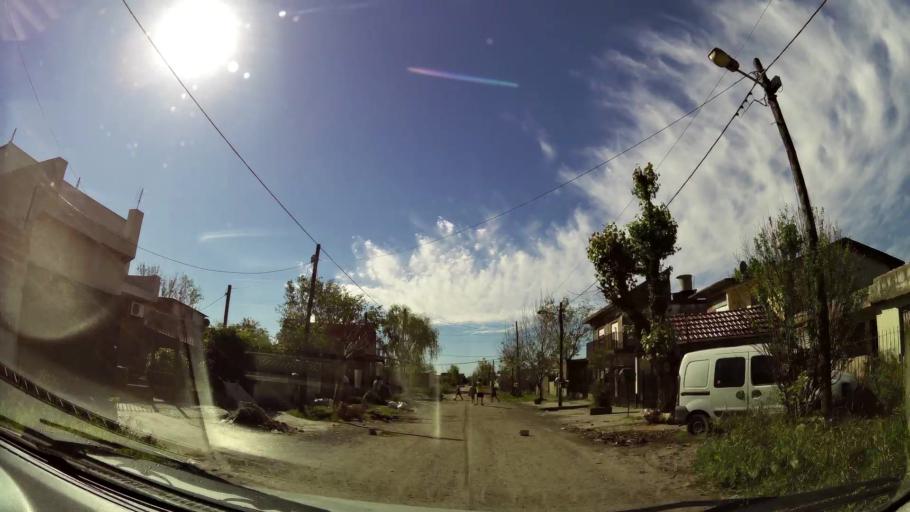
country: AR
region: Buenos Aires
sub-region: Partido de Quilmes
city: Quilmes
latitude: -34.7630
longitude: -58.3080
